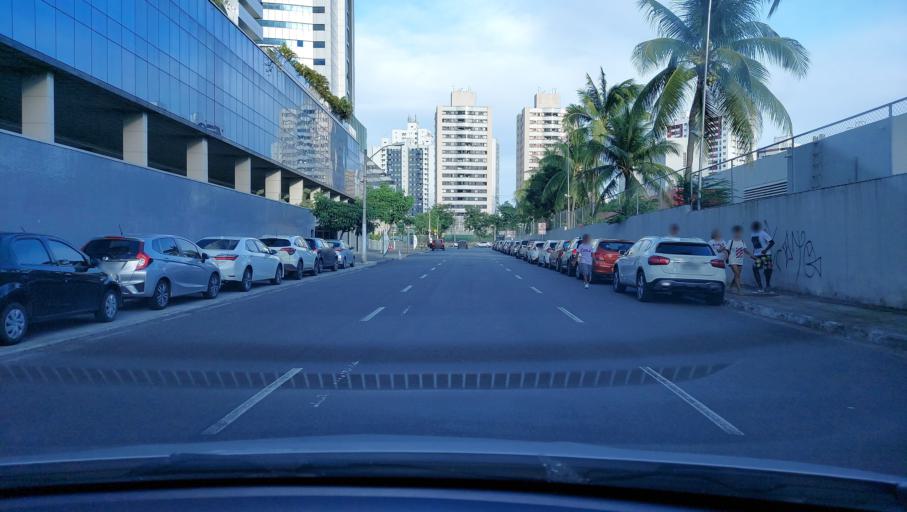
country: BR
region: Bahia
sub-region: Salvador
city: Salvador
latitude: -12.9811
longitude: -38.4518
